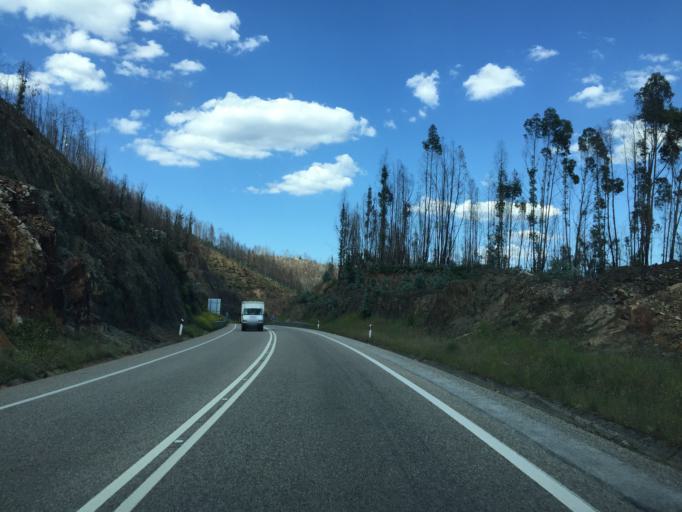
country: PT
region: Leiria
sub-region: Figueiro Dos Vinhos
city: Figueiro dos Vinhos
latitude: 39.9259
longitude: -8.3181
